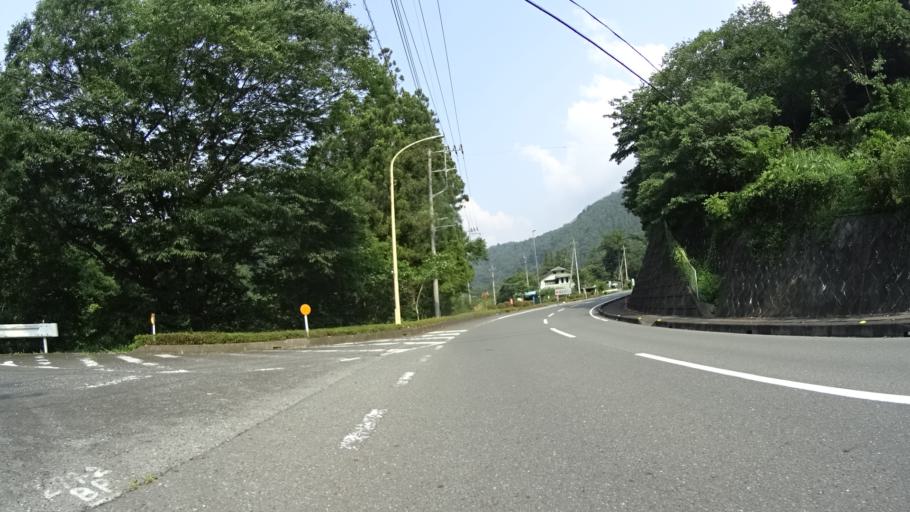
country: JP
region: Saitama
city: Chichibu
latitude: 36.0333
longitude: 138.9281
